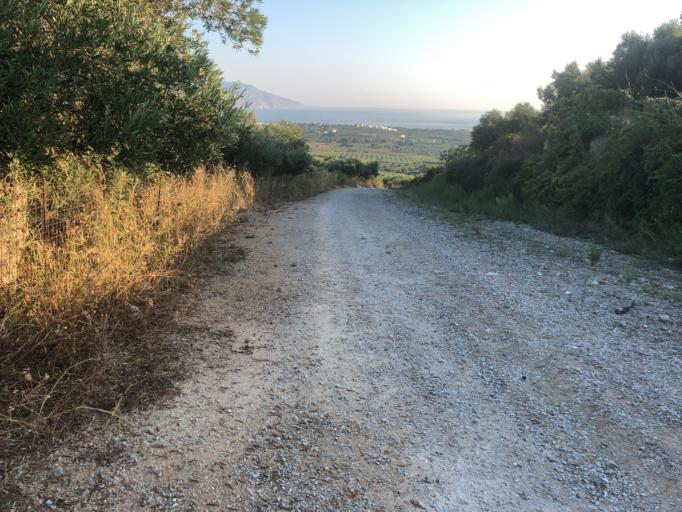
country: GR
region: Crete
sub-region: Nomos Chanias
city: Georgioupolis
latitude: 35.3340
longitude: 24.2913
